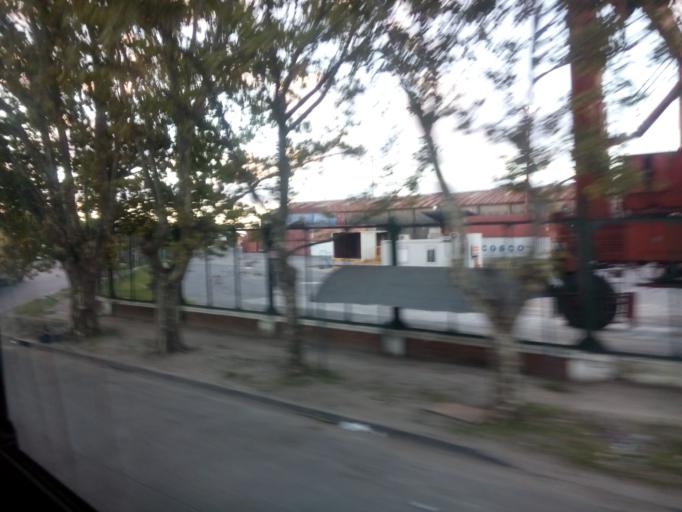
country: AR
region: Buenos Aires F.D.
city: Retiro
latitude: -34.5799
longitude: -58.3795
